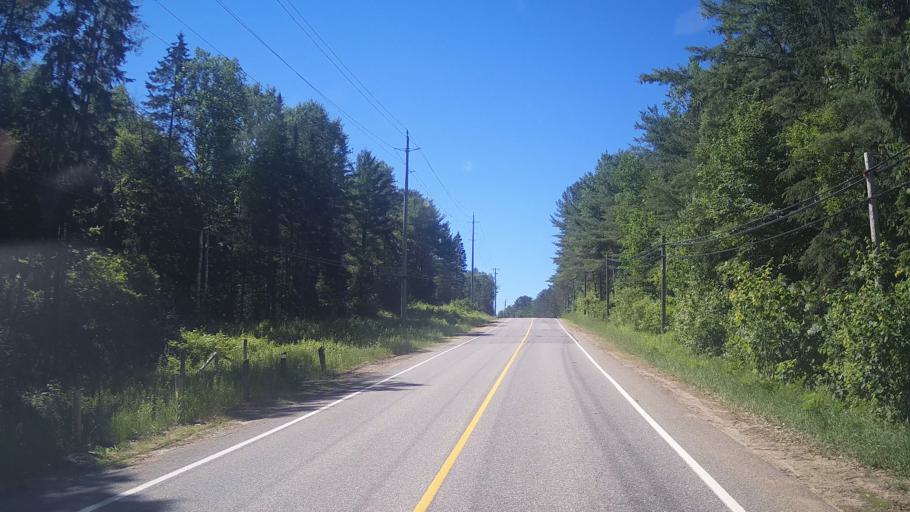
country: CA
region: Ontario
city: Huntsville
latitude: 45.3654
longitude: -79.2048
